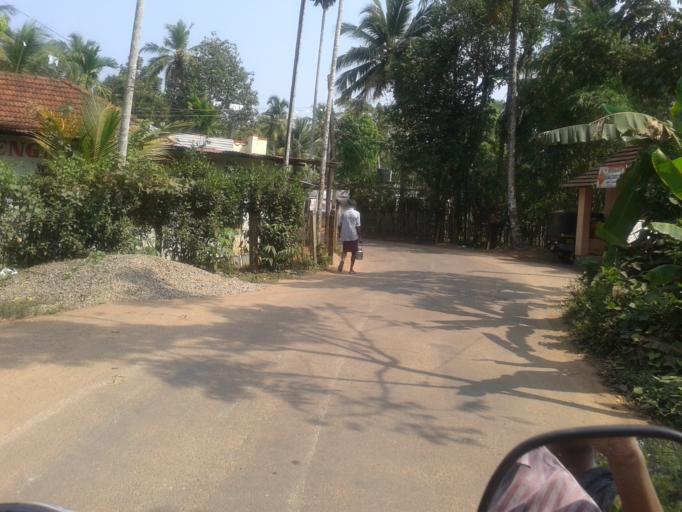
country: IN
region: Kerala
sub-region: Kottayam
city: Changanacheri
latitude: 9.4597
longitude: 76.4427
